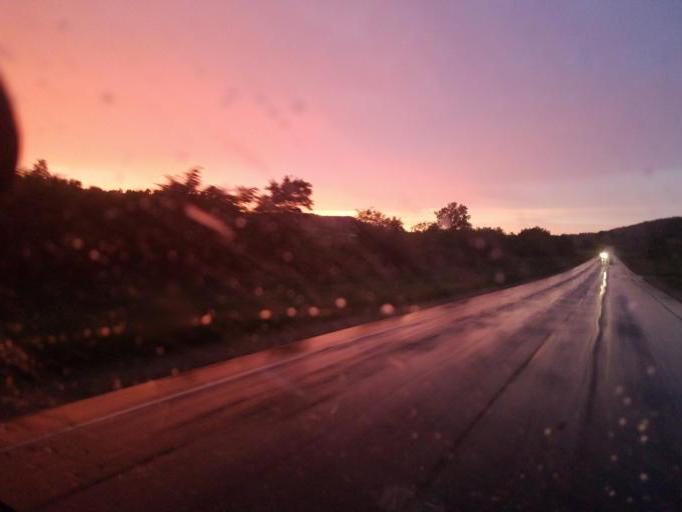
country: US
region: Wisconsin
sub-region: Vernon County
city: Hillsboro
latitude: 43.6032
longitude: -90.3528
